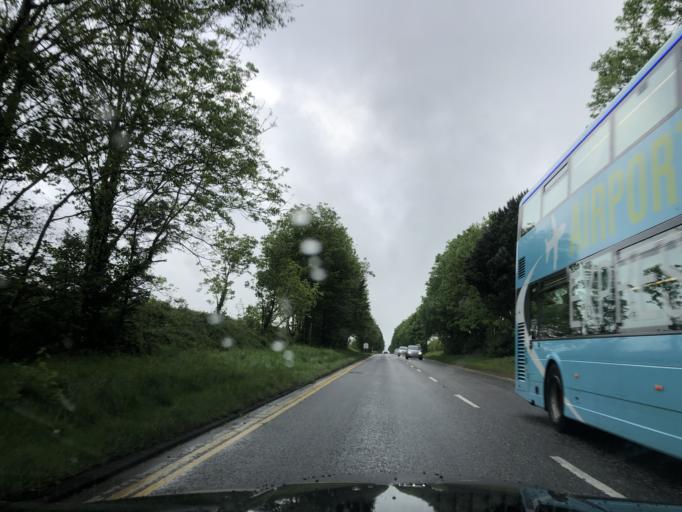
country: GB
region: Northern Ireland
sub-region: Antrim Borough
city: Antrim
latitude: 54.6664
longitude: -6.1991
